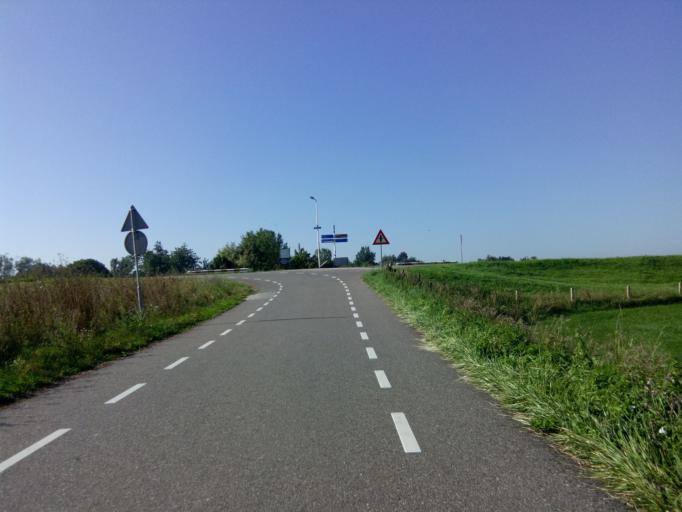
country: NL
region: Gelderland
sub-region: Gemeente Buren
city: Lienden
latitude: 51.9767
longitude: 5.4942
